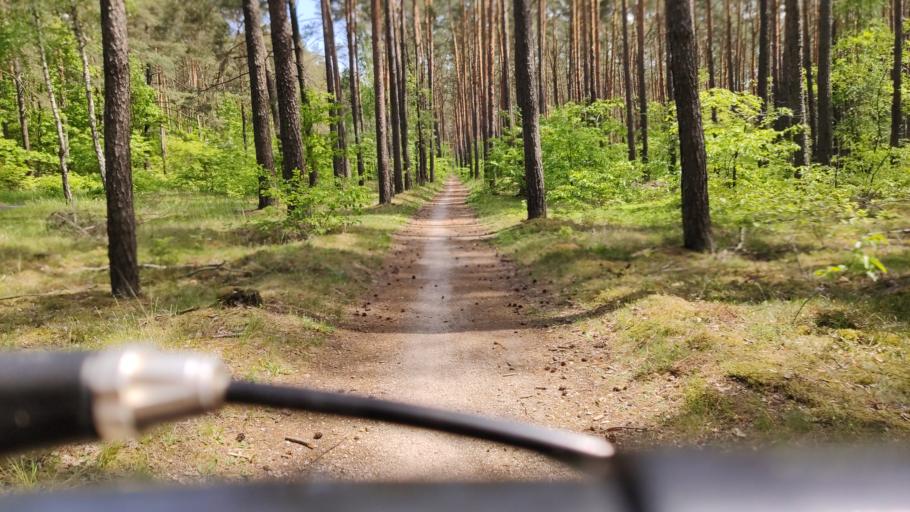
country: PL
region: Kujawsko-Pomorskie
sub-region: Wloclawek
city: Wloclawek
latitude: 52.6336
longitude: 19.1293
